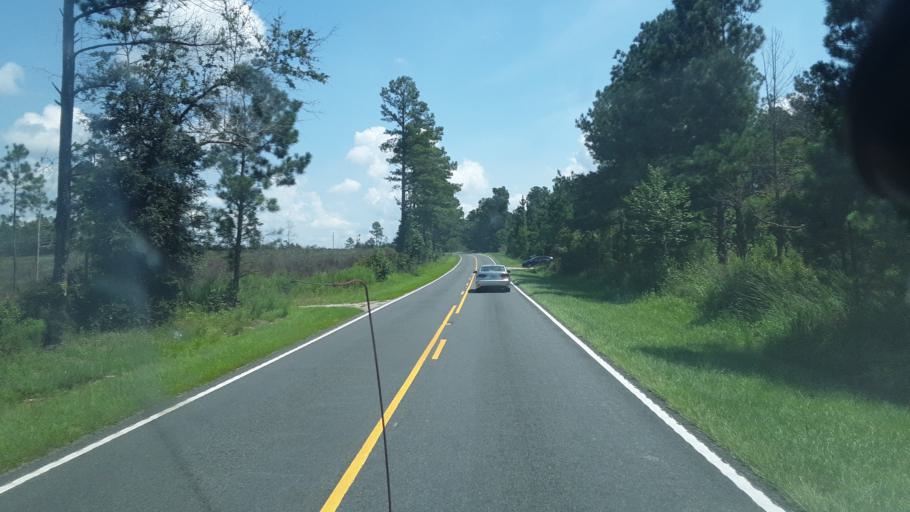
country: US
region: South Carolina
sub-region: Calhoun County
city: Oak Grove
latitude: 33.6352
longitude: -81.0095
